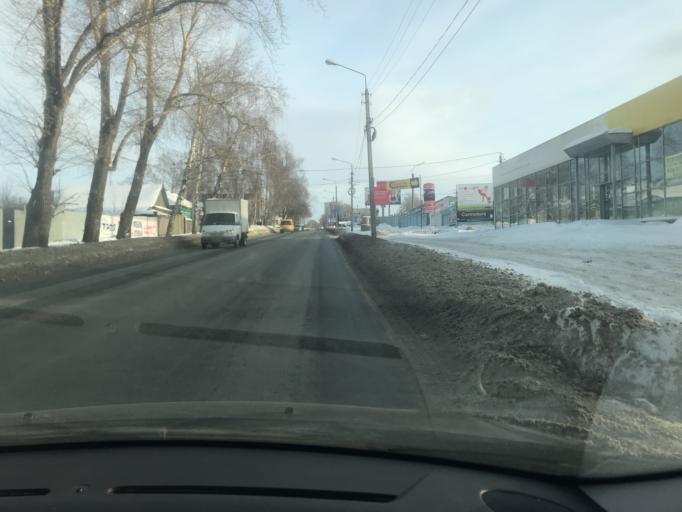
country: RU
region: Ulyanovsk
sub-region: Ulyanovskiy Rayon
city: Ulyanovsk
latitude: 54.3323
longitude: 48.3671
